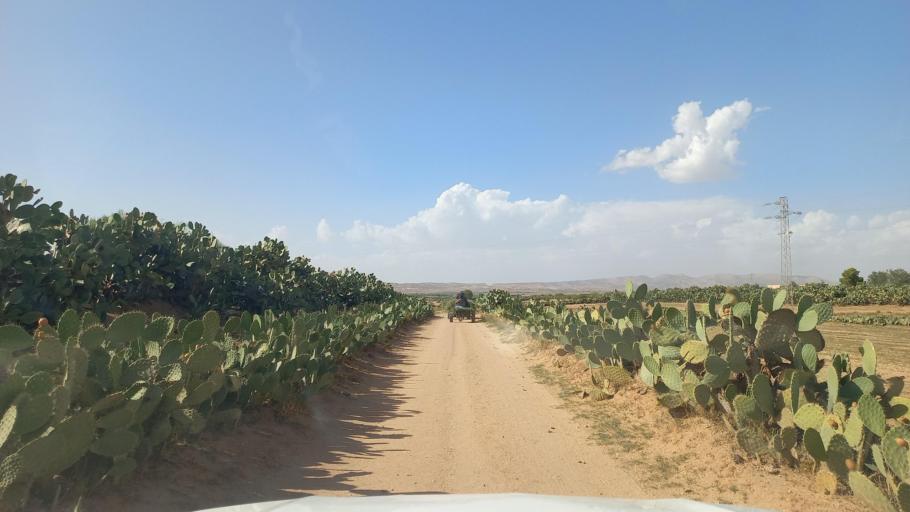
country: TN
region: Al Qasrayn
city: Sbiba
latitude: 35.3084
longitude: 9.0344
